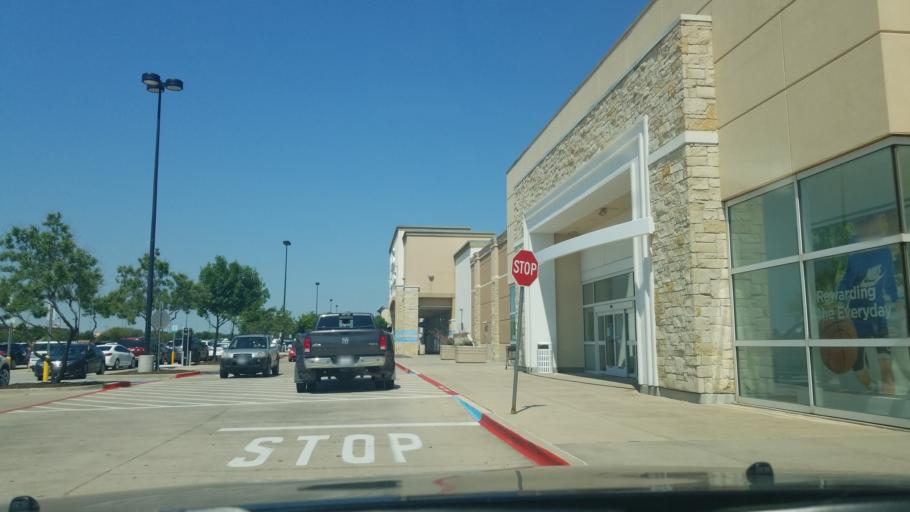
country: US
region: Texas
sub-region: Denton County
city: Denton
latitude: 33.2319
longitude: -97.1634
